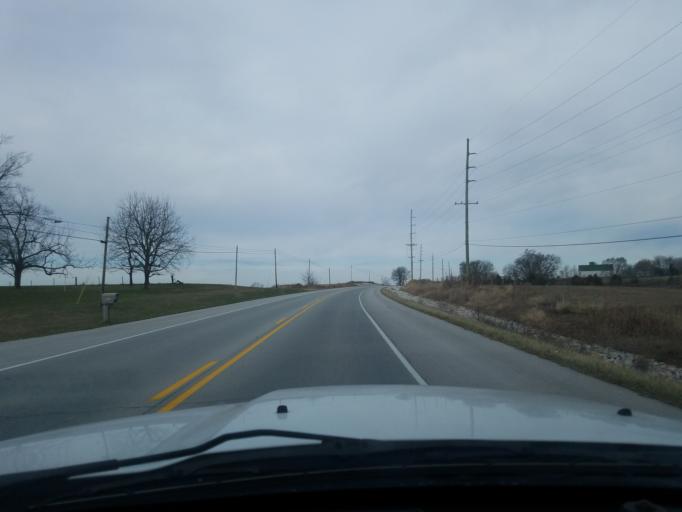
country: US
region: Indiana
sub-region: Orange County
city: Orleans
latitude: 38.6951
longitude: -86.4598
